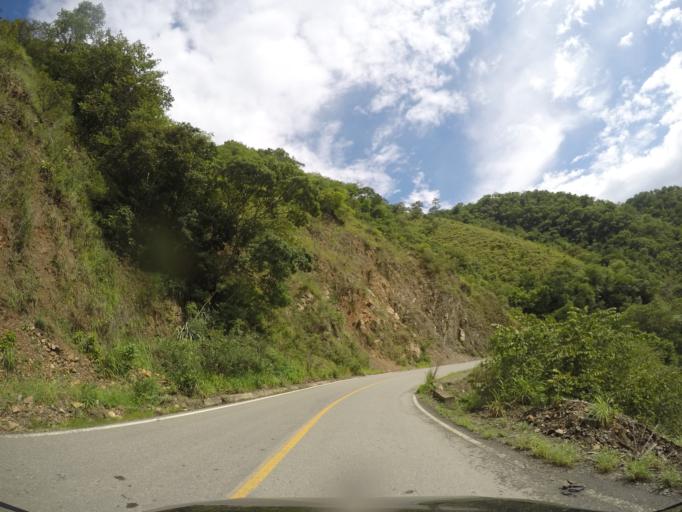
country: MX
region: Oaxaca
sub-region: San Jeronimo Coatlan
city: San Cristobal Honduras
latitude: 16.3718
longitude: -97.0829
